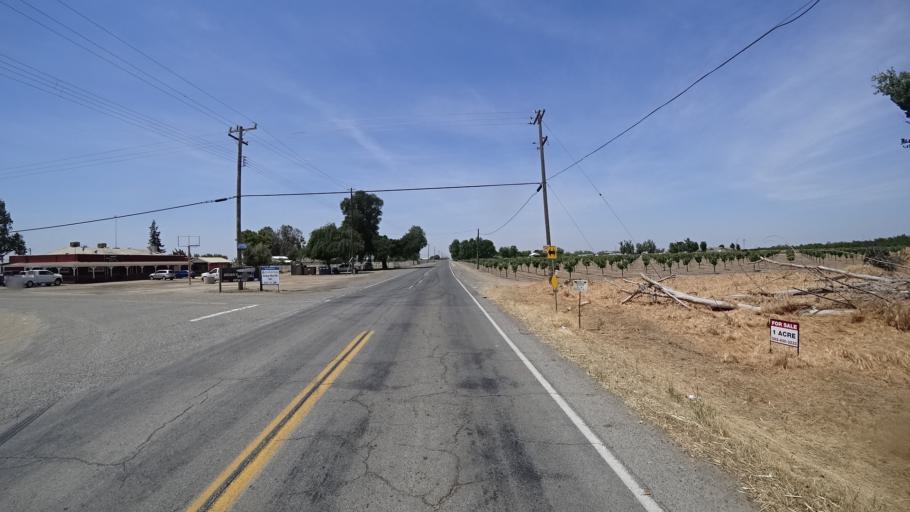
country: US
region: California
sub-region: Fresno County
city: Riverdale
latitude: 36.4021
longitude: -119.8092
